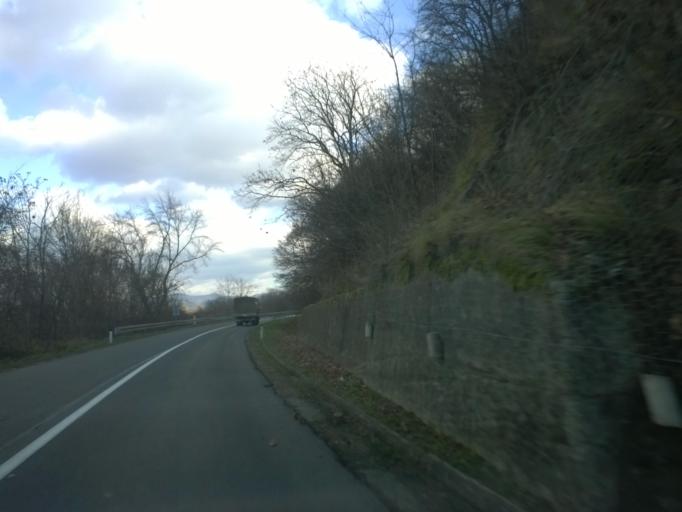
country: RO
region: Caras-Severin
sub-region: Comuna Berzasca
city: Liubcova
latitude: 44.6458
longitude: 21.8346
